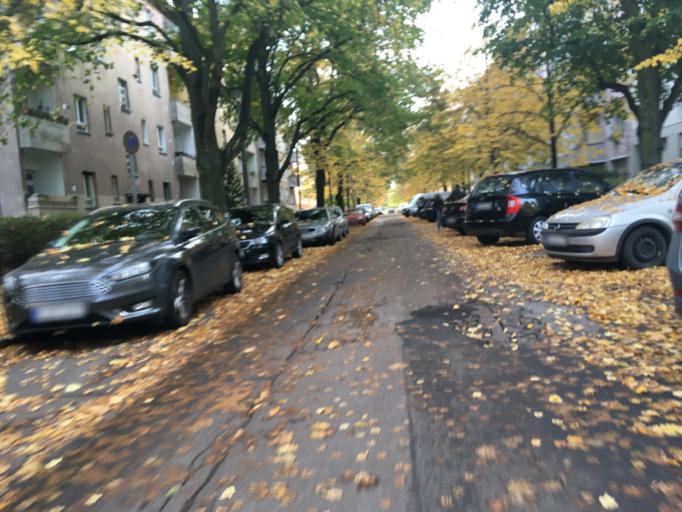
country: DE
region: Berlin
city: Pankow
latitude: 52.5640
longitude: 13.4009
